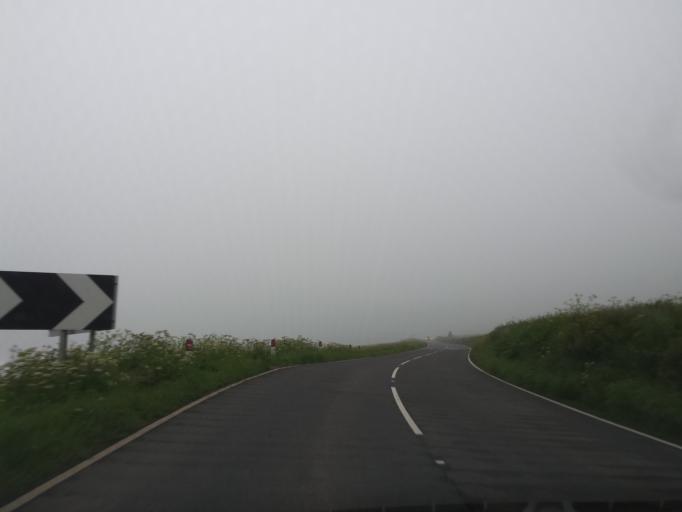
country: GB
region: Scotland
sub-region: Highland
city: Thurso
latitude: 58.2242
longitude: -3.4549
